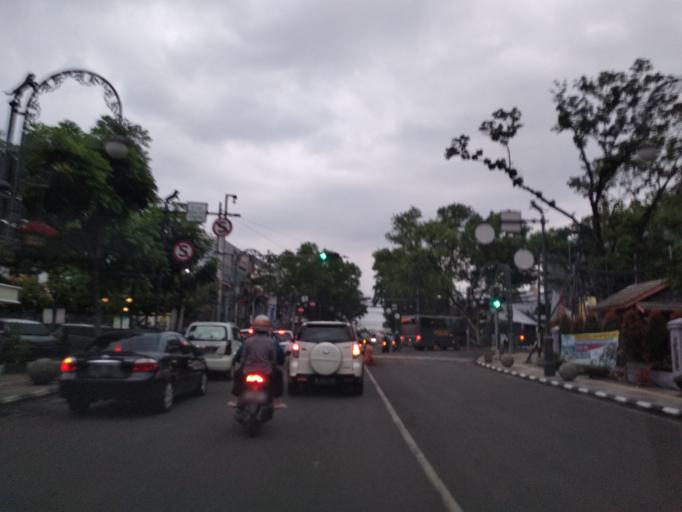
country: ID
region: West Java
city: Bandung
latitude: -6.9070
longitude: 107.6113
